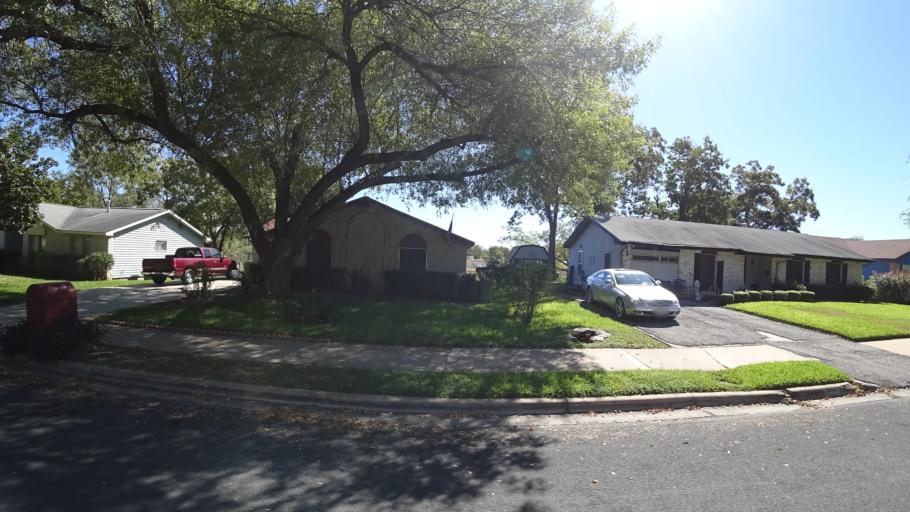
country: US
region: Texas
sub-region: Travis County
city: Austin
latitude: 30.2862
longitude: -97.6612
